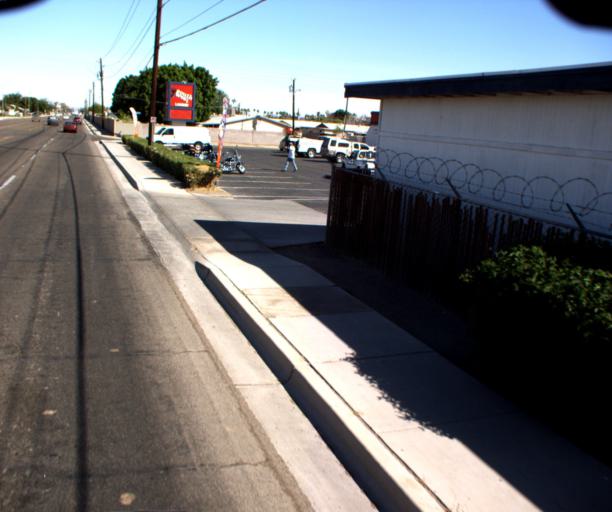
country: US
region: Arizona
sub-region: Yuma County
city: Yuma
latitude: 32.6924
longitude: -114.6504
